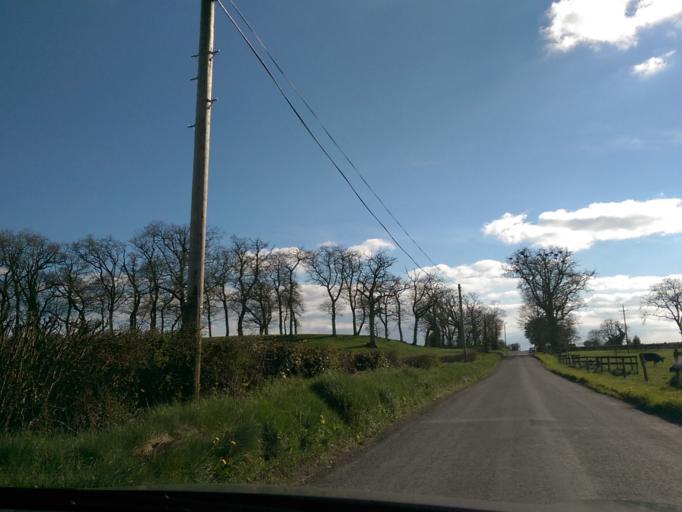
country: IE
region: Leinster
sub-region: Uibh Fhaili
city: Birr
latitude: 53.0749
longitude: -7.9357
